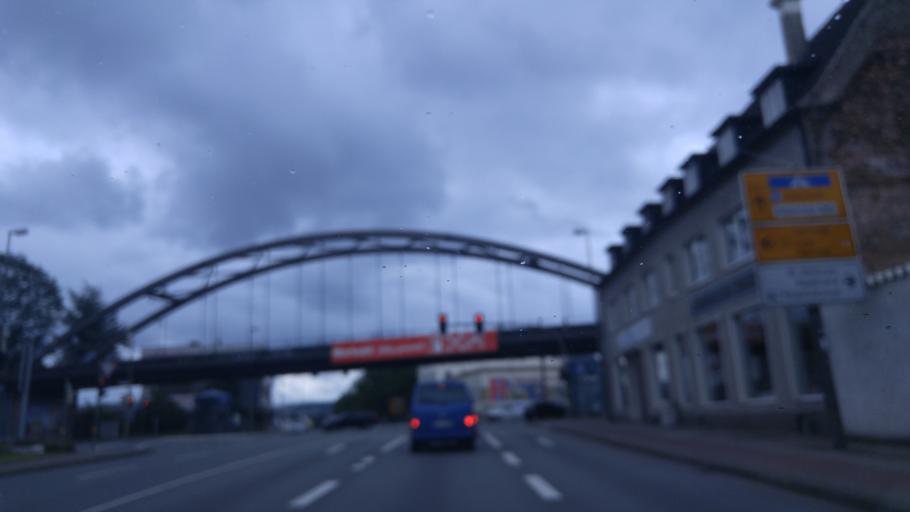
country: DE
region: North Rhine-Westphalia
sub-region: Regierungsbezirk Detmold
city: Bielefeld
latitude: 52.0339
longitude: 8.5431
